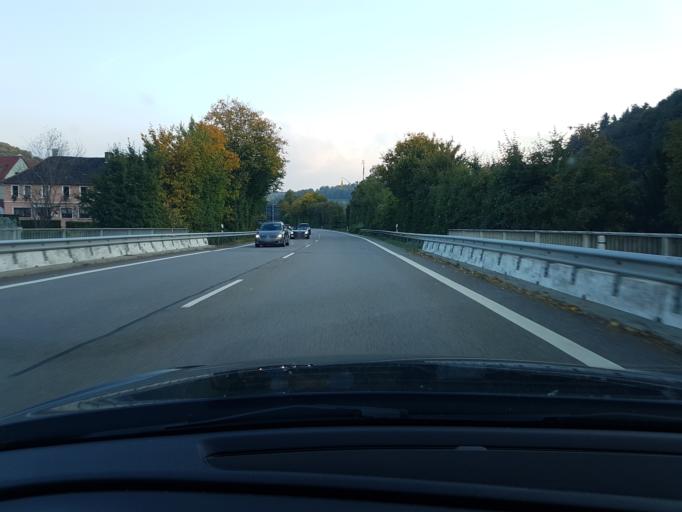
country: DE
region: Baden-Wuerttemberg
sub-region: Karlsruhe Region
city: Neckargerach
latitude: 49.3992
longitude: 9.0678
